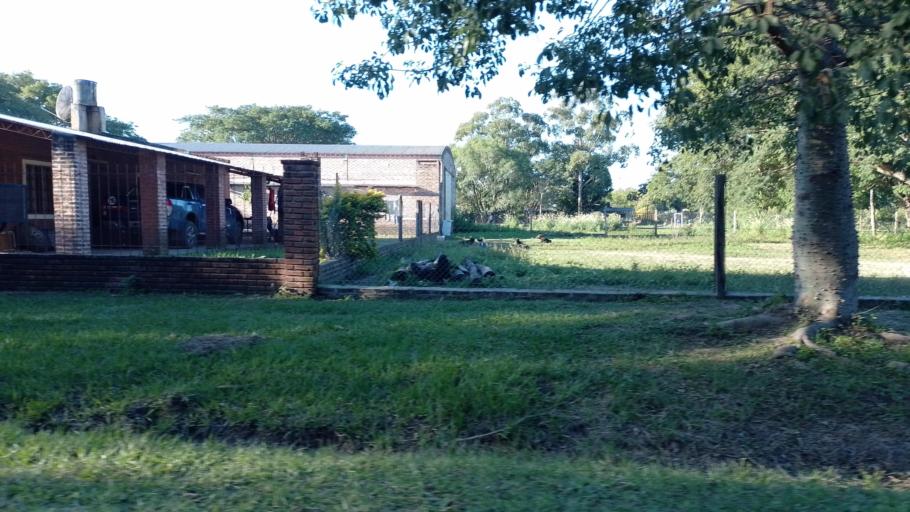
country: AR
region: Chaco
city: Colonia Benitez
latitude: -27.3289
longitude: -58.9471
